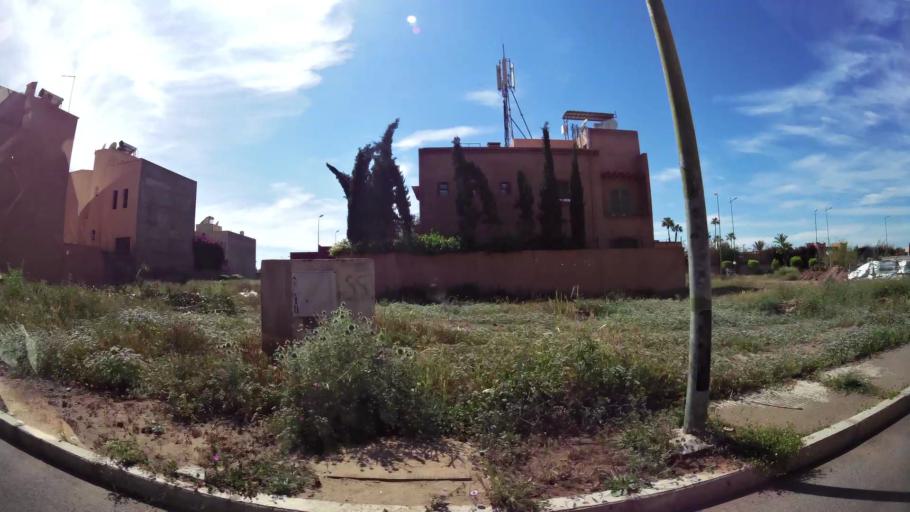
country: MA
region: Marrakech-Tensift-Al Haouz
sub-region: Marrakech
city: Marrakesh
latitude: 31.6575
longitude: -8.0590
